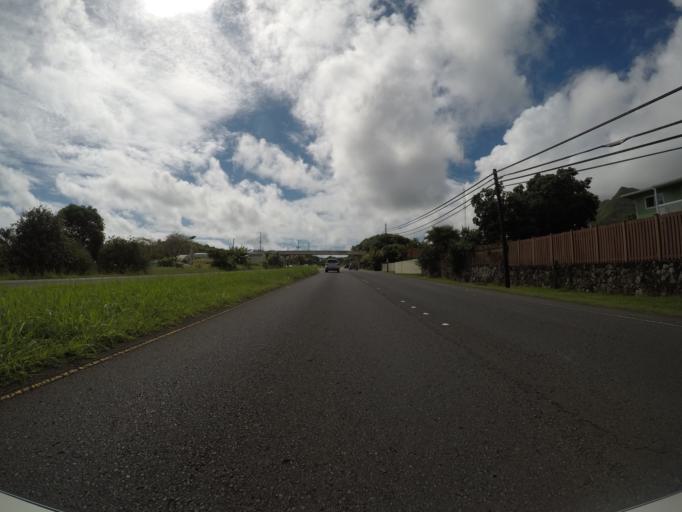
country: US
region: Hawaii
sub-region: Honolulu County
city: Maunawili
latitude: 21.3790
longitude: -157.7529
